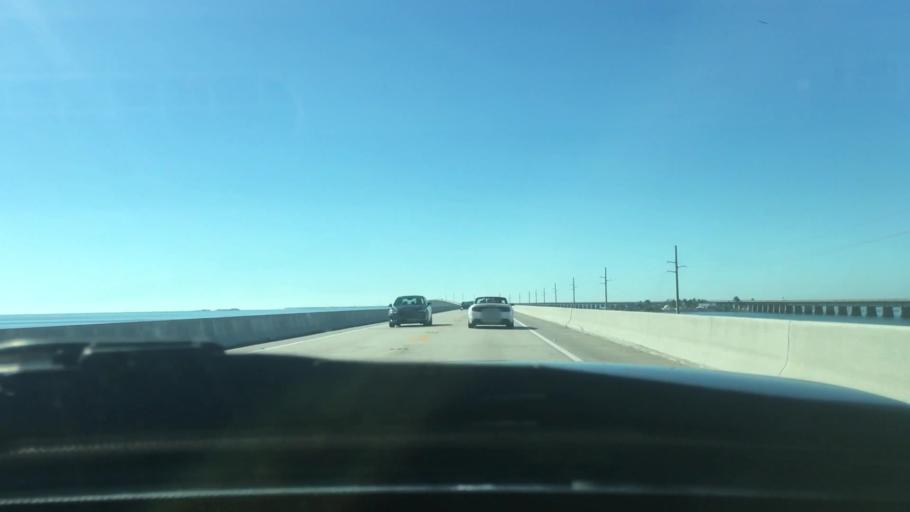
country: US
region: Florida
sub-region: Monroe County
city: Marathon
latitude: 24.7043
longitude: -81.1468
